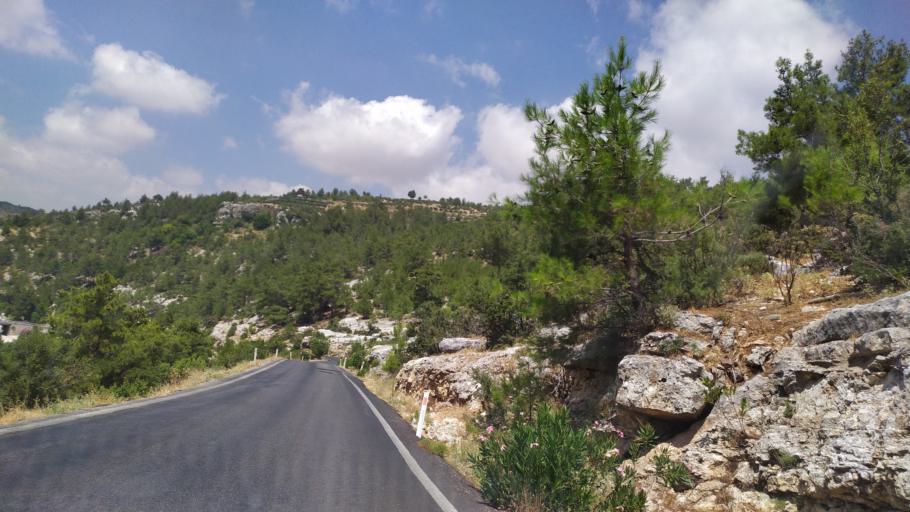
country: TR
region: Mersin
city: Gulnar
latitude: 36.2755
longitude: 33.3835
